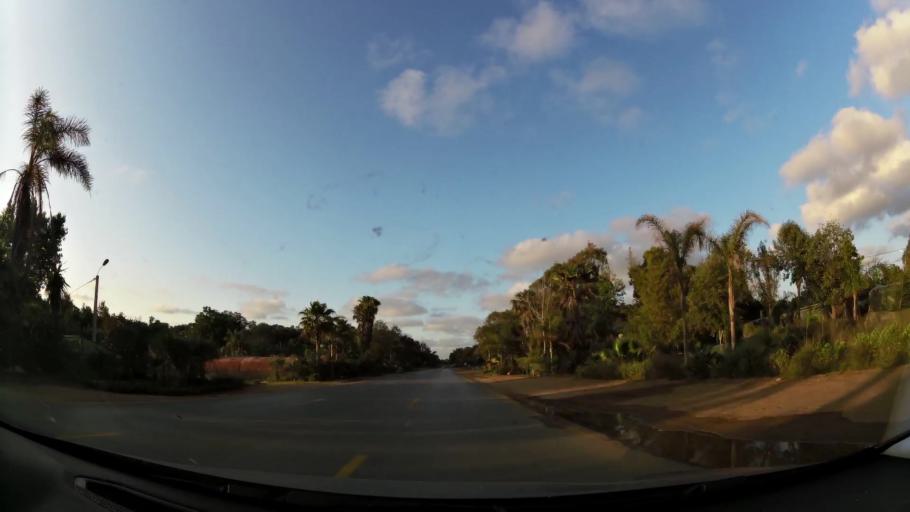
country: MA
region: Gharb-Chrarda-Beni Hssen
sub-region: Kenitra Province
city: Kenitra
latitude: 34.2125
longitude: -6.6692
